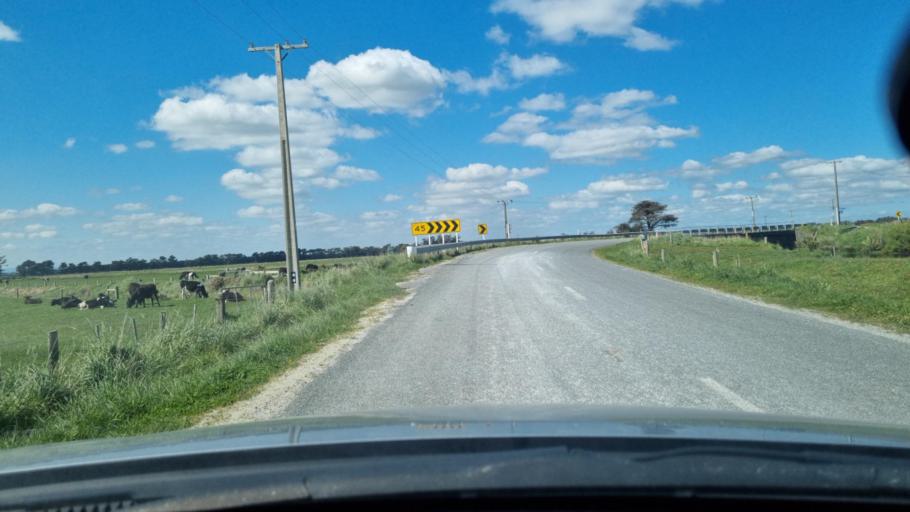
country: NZ
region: Southland
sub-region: Invercargill City
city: Invercargill
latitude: -46.3908
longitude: 168.2607
